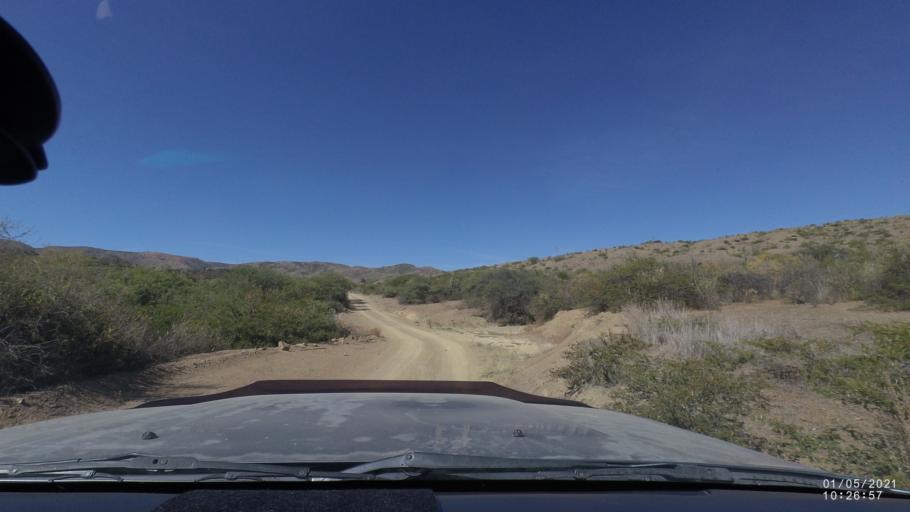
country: BO
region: Cochabamba
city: Capinota
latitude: -17.5826
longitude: -66.1917
